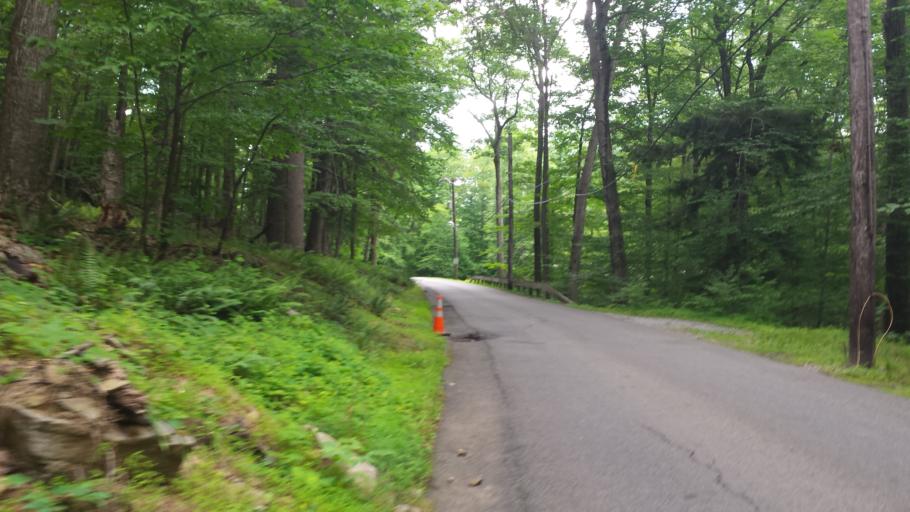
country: US
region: New York
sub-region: Putnam County
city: Peach Lake
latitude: 41.3081
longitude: -73.5642
